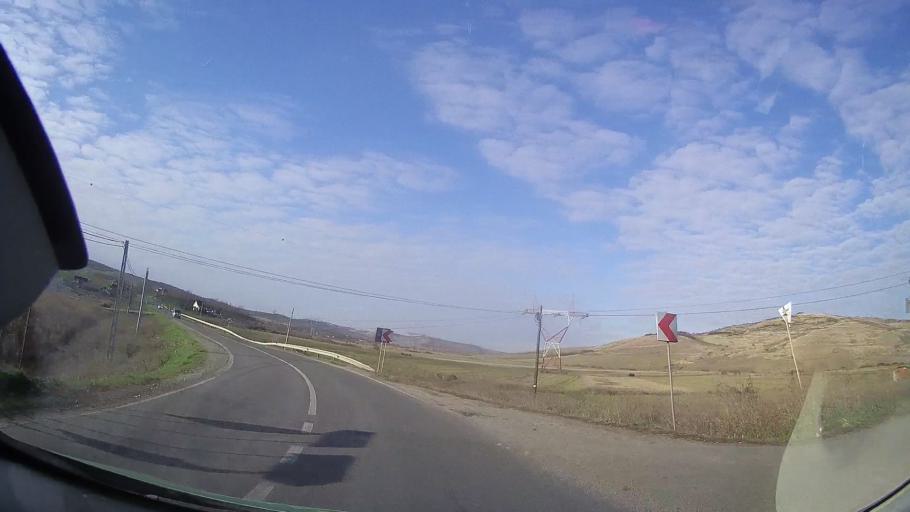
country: RO
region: Cluj
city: Caianu Mic
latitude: 46.8119
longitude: 23.8723
